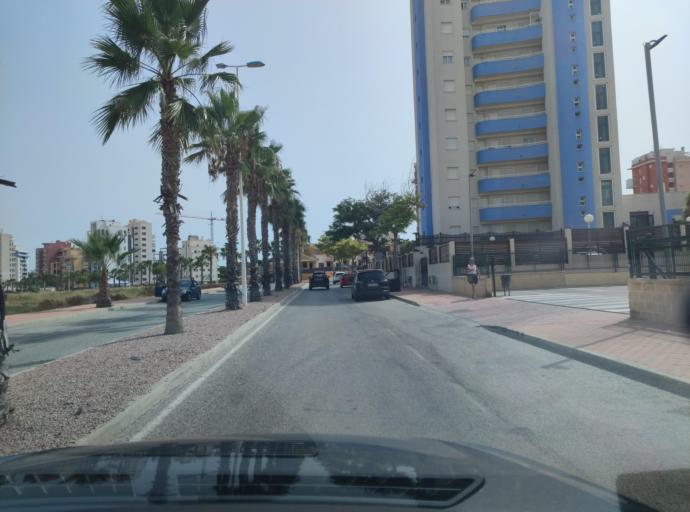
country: ES
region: Valencia
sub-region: Provincia de Alicante
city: Guardamar del Segura
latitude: 38.0973
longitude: -0.6568
